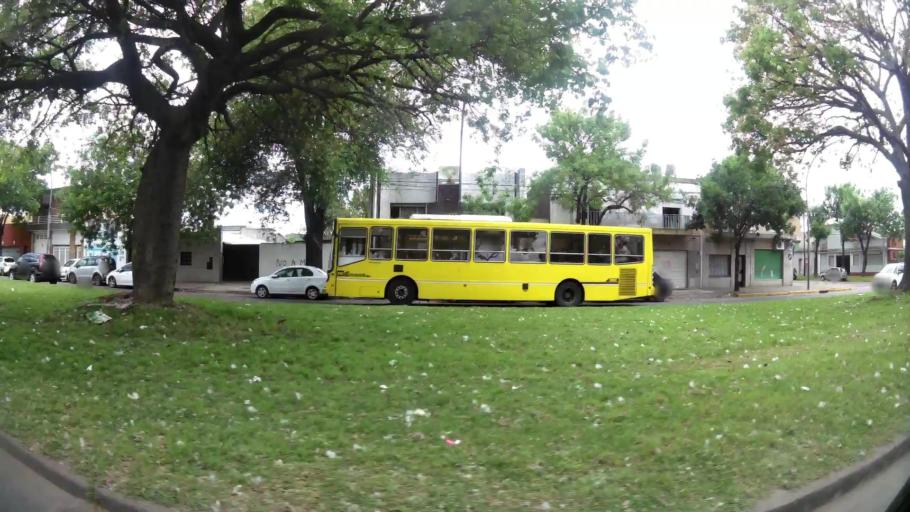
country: AR
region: Santa Fe
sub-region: Departamento de Rosario
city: Rosario
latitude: -32.9766
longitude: -60.6597
